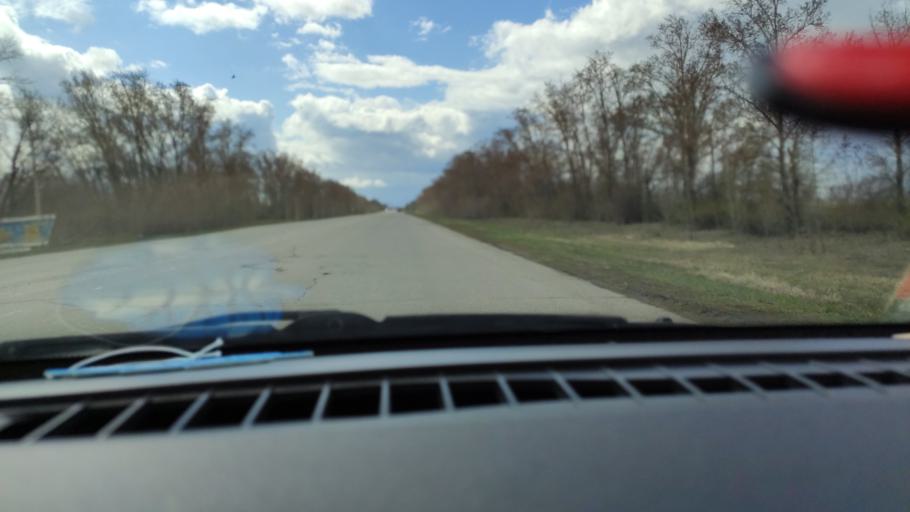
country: RU
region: Samara
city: Tol'yatti
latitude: 53.5899
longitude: 49.4060
